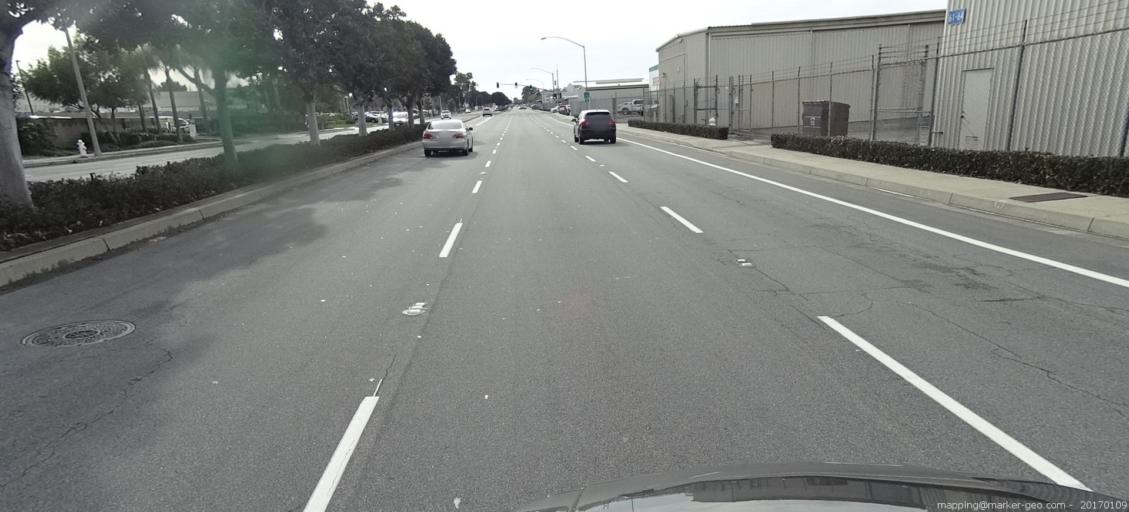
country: US
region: California
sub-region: Orange County
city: Irvine
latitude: 33.6689
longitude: -117.8687
